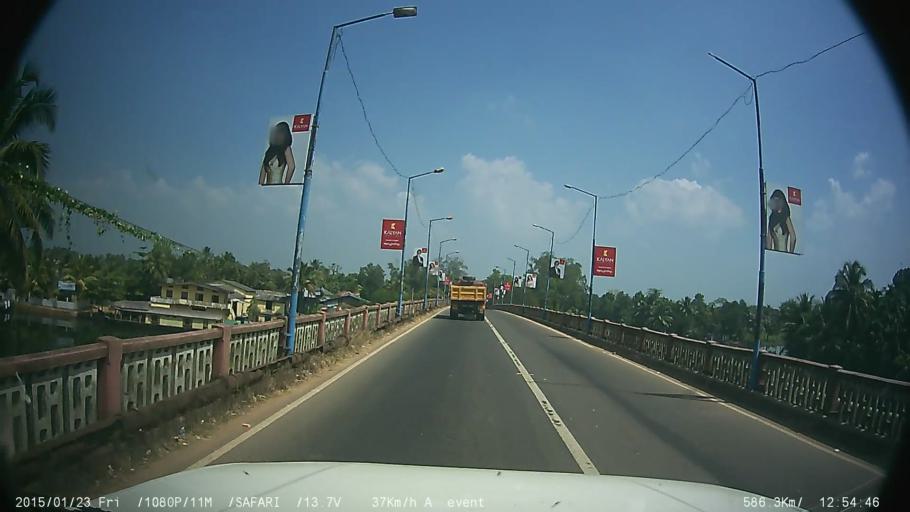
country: IN
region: Kerala
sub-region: Kottayam
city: Changanacheri
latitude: 9.4194
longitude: 76.4919
